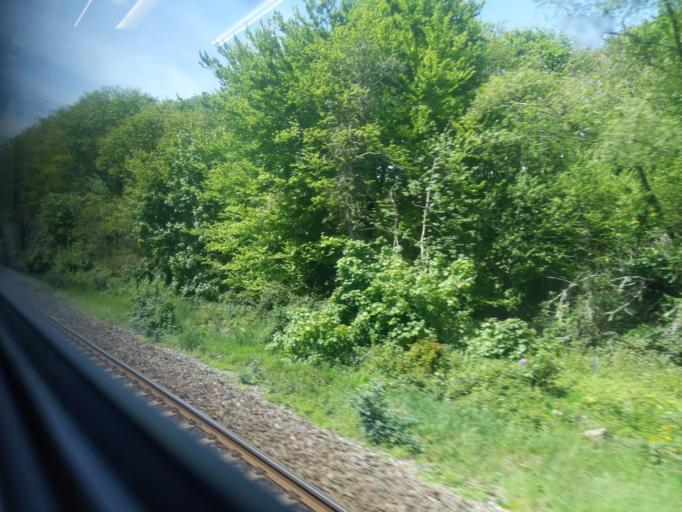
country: GB
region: England
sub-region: Cornwall
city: St Austell
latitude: 50.3436
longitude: -4.8071
